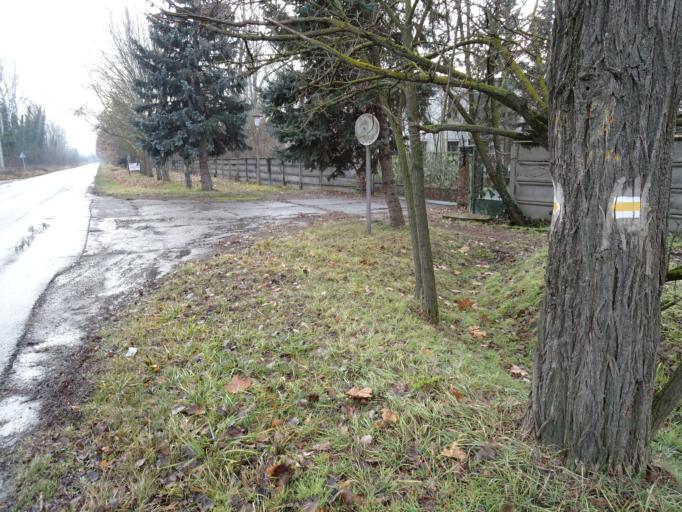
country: HU
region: Bacs-Kiskun
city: Szabadszallas
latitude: 46.8934
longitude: 19.2193
